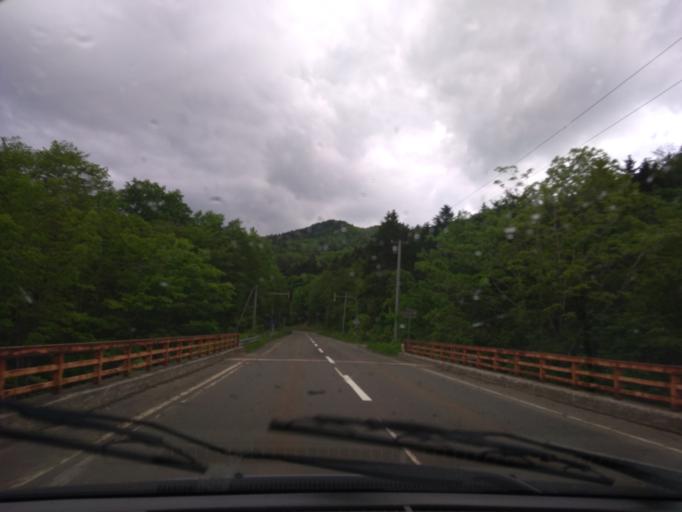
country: JP
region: Hokkaido
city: Shimo-furano
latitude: 43.1214
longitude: 142.4010
